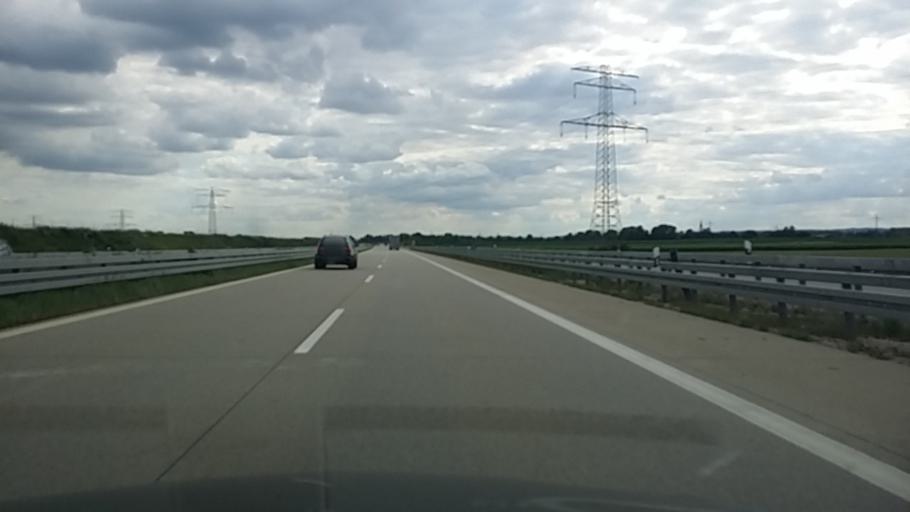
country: DE
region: Bavaria
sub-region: Lower Bavaria
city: Essenbach
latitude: 48.6004
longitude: 12.2288
